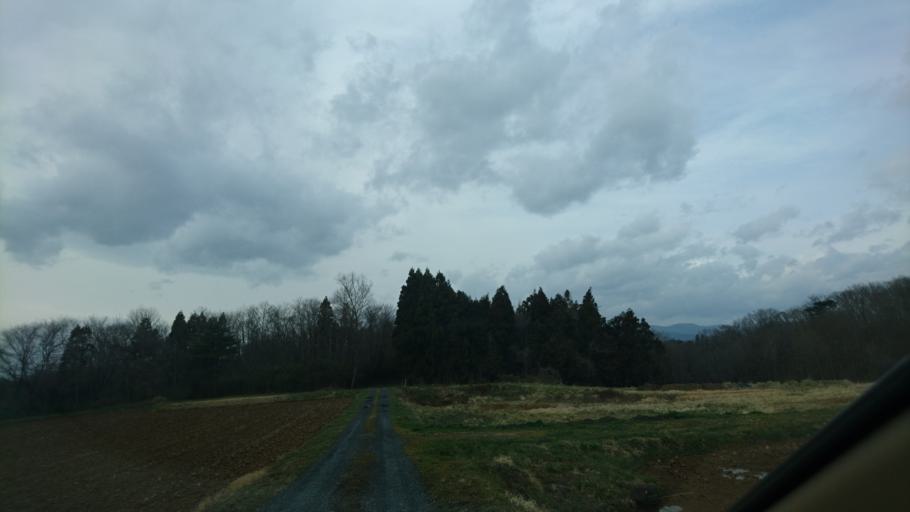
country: JP
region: Iwate
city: Ichinoseki
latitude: 38.8945
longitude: 141.1619
